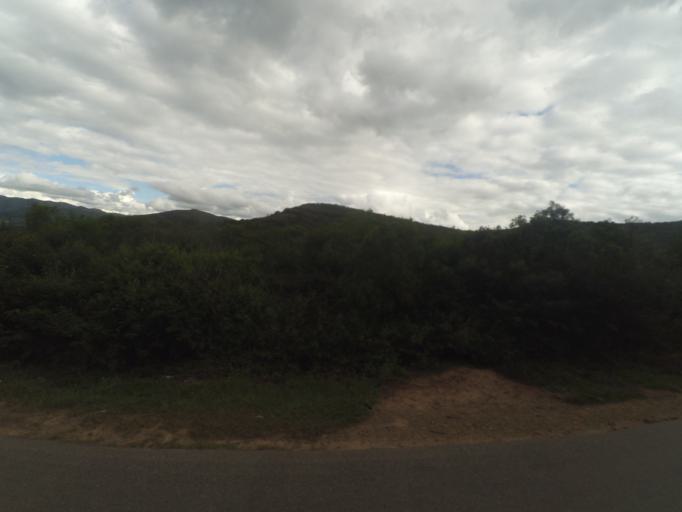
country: BO
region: Santa Cruz
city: Samaipata
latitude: -18.1736
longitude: -63.8484
